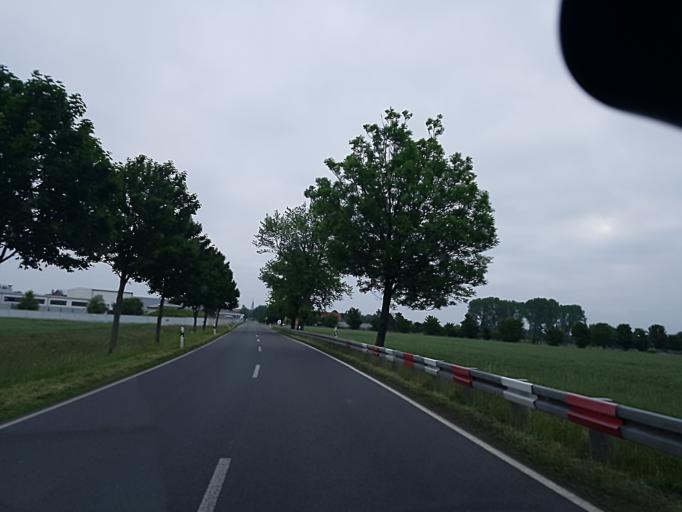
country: DE
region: Brandenburg
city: Doberlug-Kirchhain
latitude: 51.6033
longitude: 13.5363
